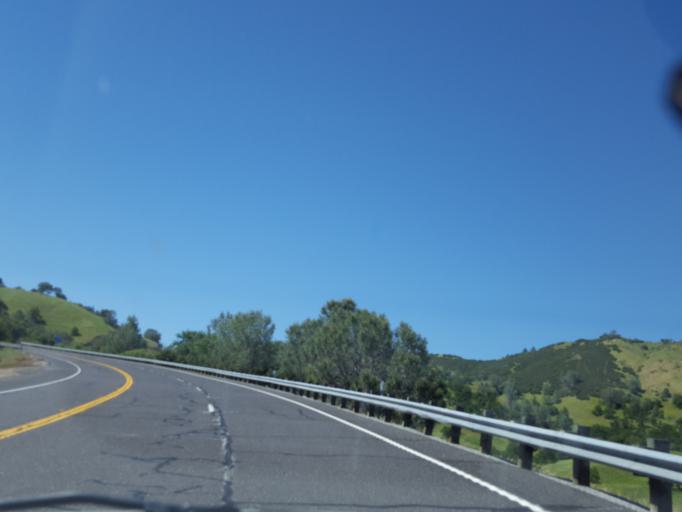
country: US
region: California
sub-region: Calaveras County
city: Angels Camp
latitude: 38.0095
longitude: -120.5051
